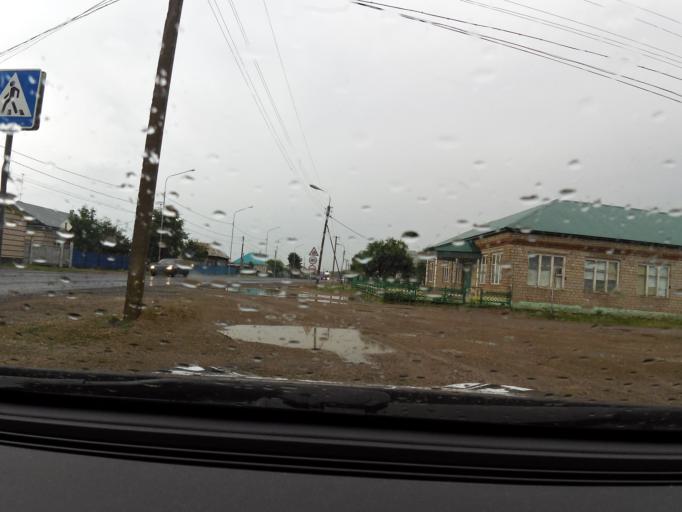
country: RU
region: Bashkortostan
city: Semiletka
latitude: 55.4701
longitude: 54.6027
